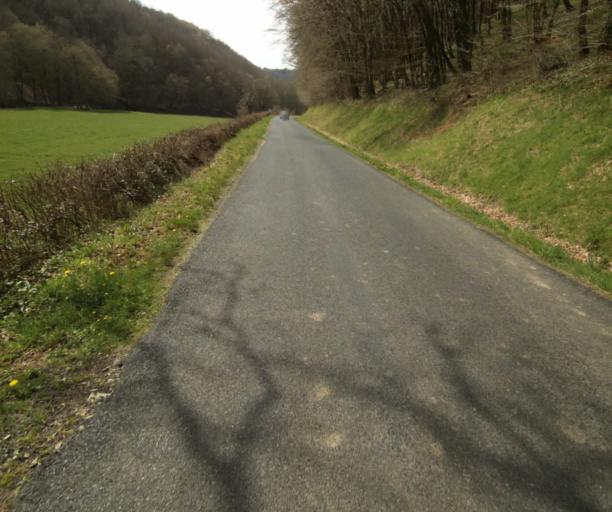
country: FR
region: Limousin
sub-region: Departement de la Correze
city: Naves
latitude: 45.3404
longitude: 1.7992
